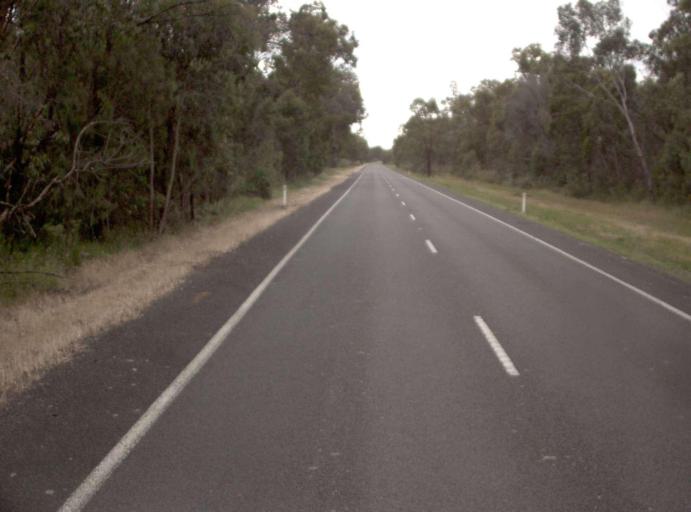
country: AU
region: Victoria
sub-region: Wellington
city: Sale
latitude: -38.3576
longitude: 146.9942
